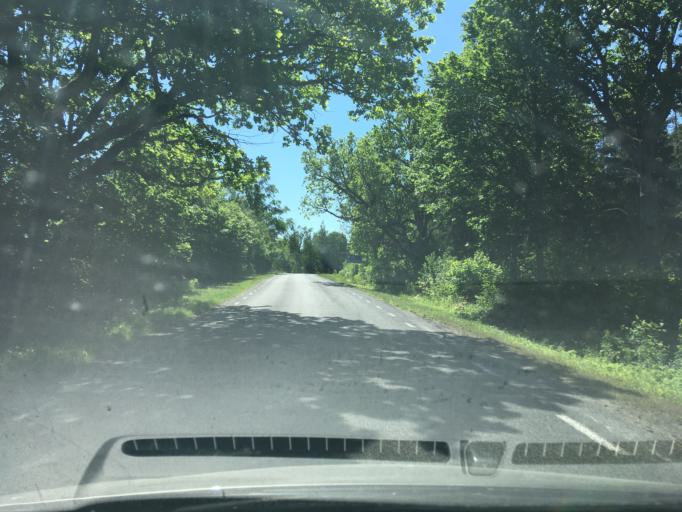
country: EE
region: Raplamaa
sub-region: Kohila vald
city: Kohila
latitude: 59.1227
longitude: 24.8370
